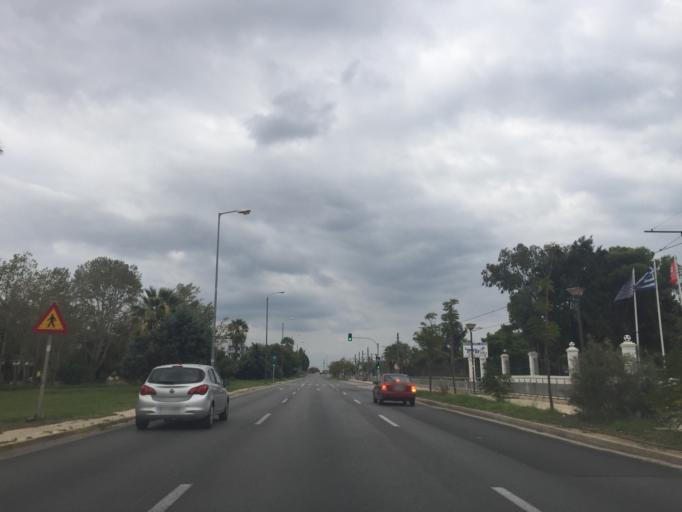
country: GR
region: Attica
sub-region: Nomarchia Athinas
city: Glyfada
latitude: 37.8521
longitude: 23.7521
